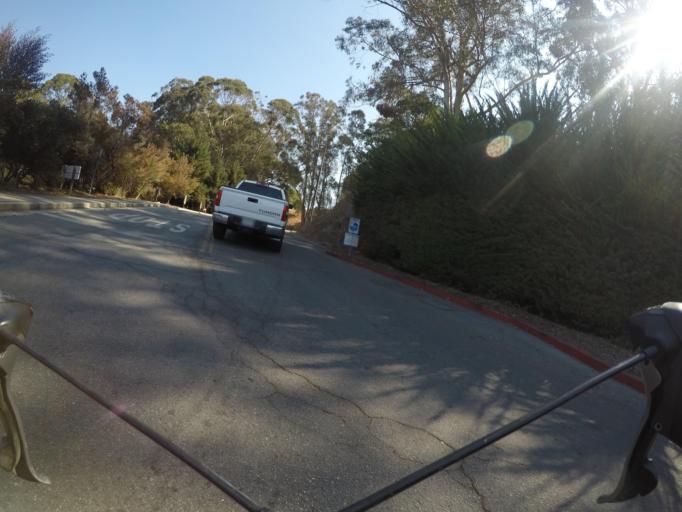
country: US
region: California
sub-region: Santa Cruz County
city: Twin Lakes
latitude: 36.9734
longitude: -121.9981
